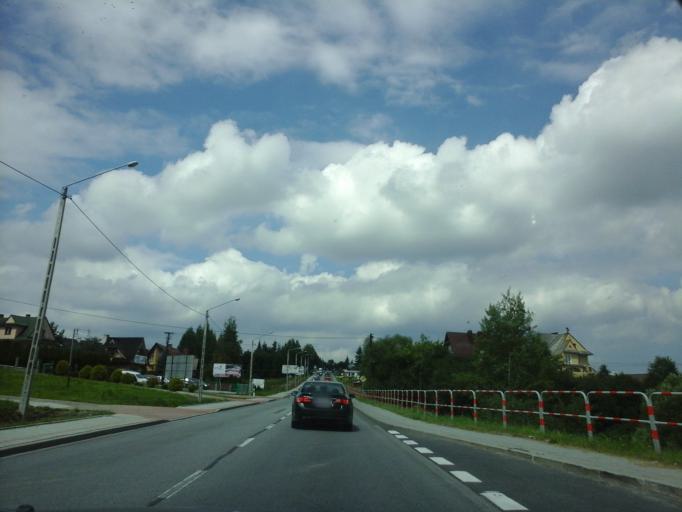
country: PL
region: Lesser Poland Voivodeship
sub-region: Powiat nowotarski
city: Nowy Targ
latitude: 49.4936
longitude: 20.0098
